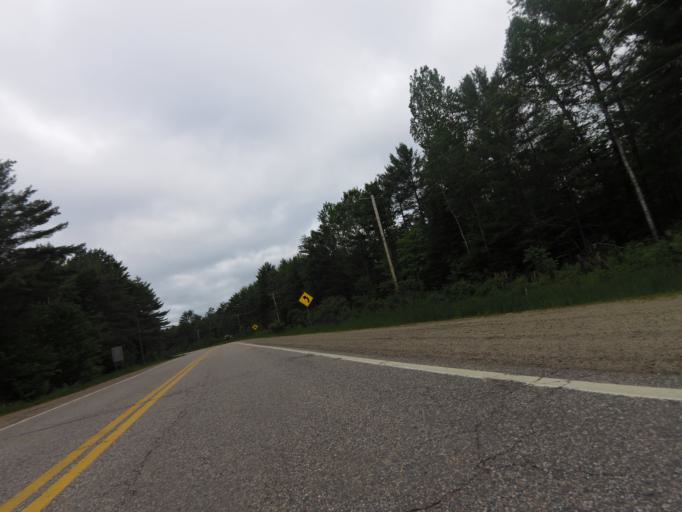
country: CA
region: Quebec
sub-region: Outaouais
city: Shawville
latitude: 45.8589
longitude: -76.4202
